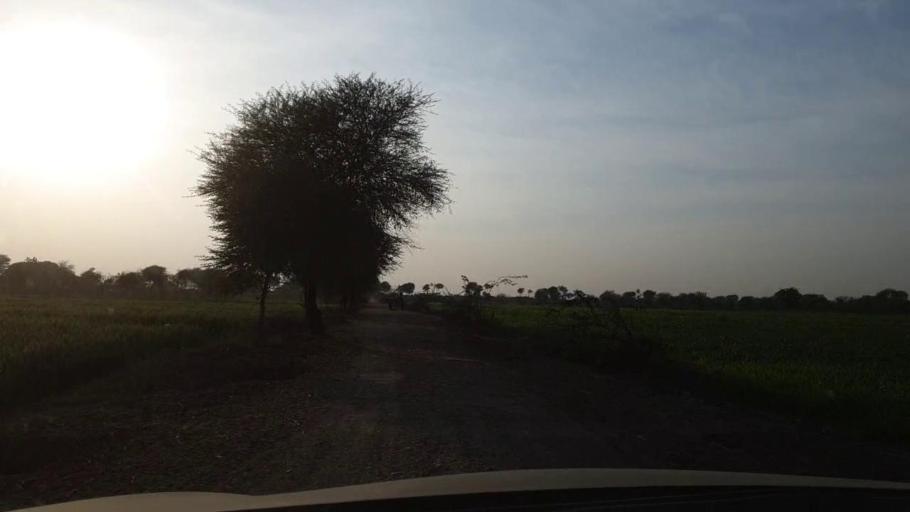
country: PK
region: Sindh
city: Tando Adam
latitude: 25.7054
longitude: 68.7397
